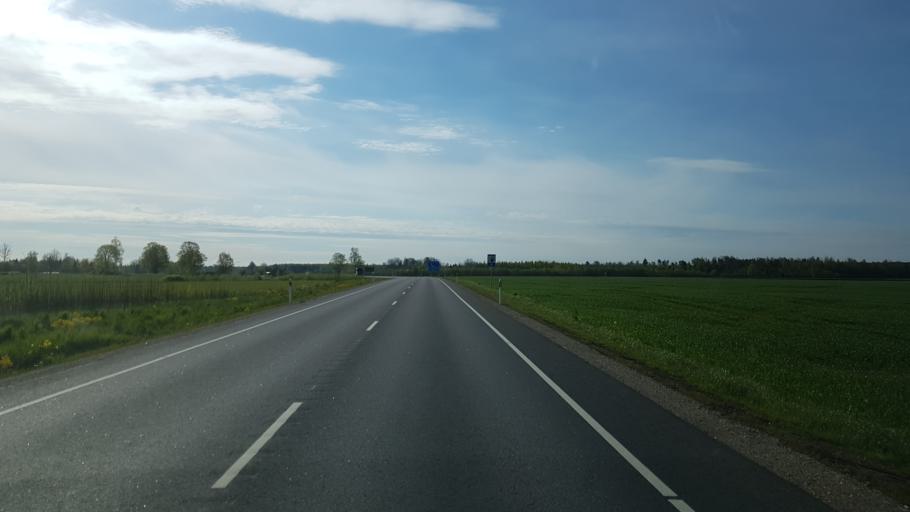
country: EE
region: Viljandimaa
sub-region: Moisakuela linn
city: Moisakula
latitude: 58.1166
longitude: 25.1903
